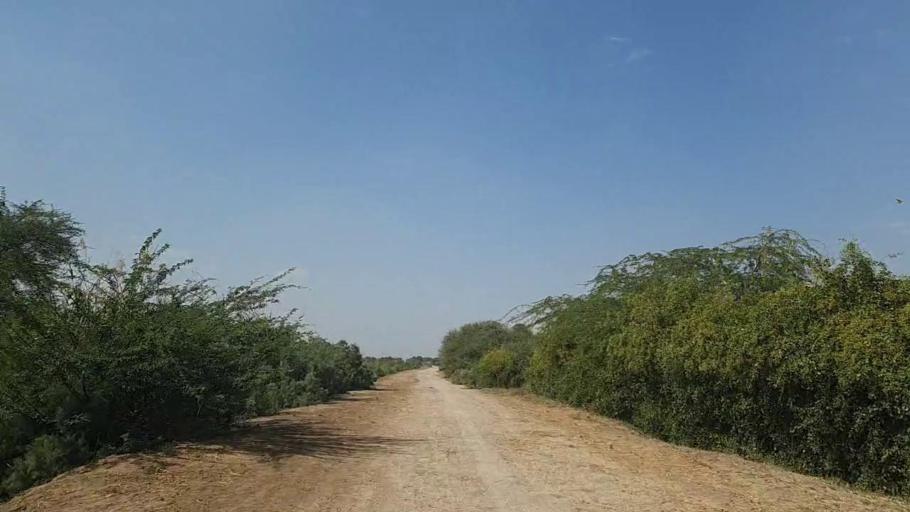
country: PK
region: Sindh
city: Jati
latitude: 24.5132
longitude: 68.2949
